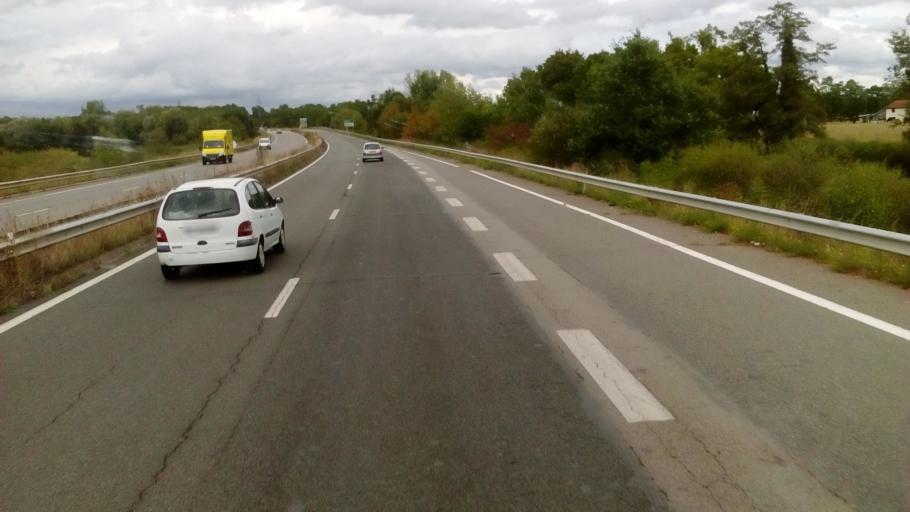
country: FR
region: Rhone-Alpes
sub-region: Departement de la Loire
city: Le Coteau
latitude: 46.0374
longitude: 4.0996
